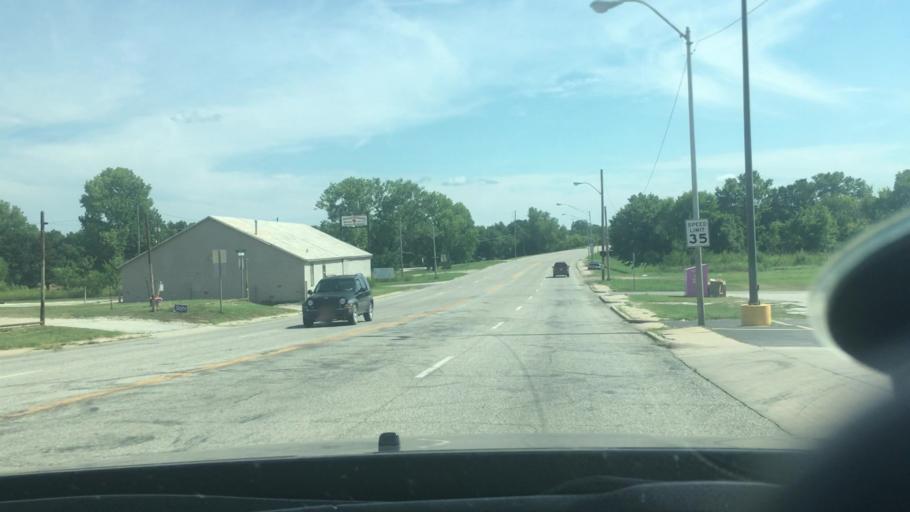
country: US
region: Oklahoma
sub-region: Seminole County
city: Seminole
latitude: 35.2234
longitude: -96.6711
